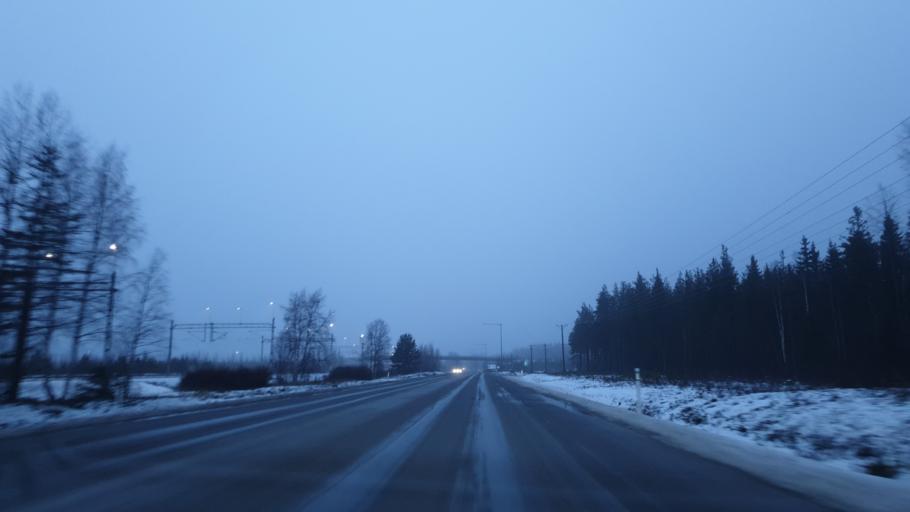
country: SE
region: Vaesterbotten
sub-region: Umea Kommun
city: Umea
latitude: 63.7868
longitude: 20.3173
